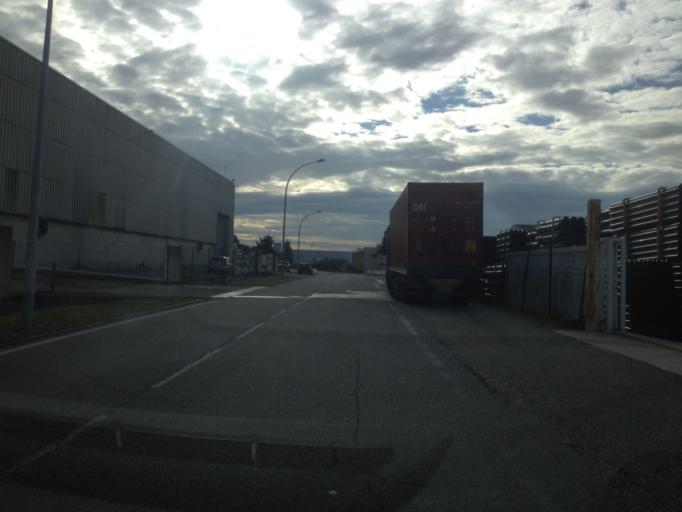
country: FR
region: Provence-Alpes-Cote d'Azur
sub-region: Departement du Vaucluse
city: Sorgues
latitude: 44.0127
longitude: 4.8890
